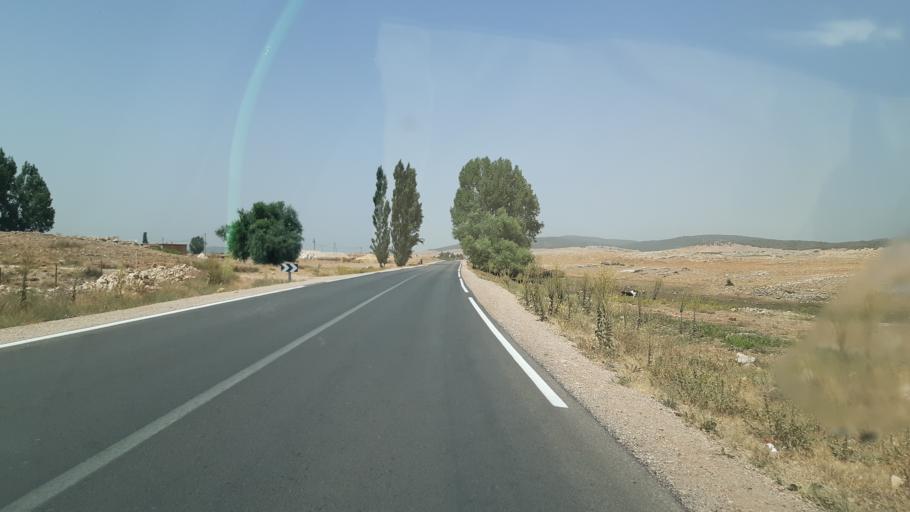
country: MA
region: Meknes-Tafilalet
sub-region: Ifrane
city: Ifrane
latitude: 33.5850
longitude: -5.0898
